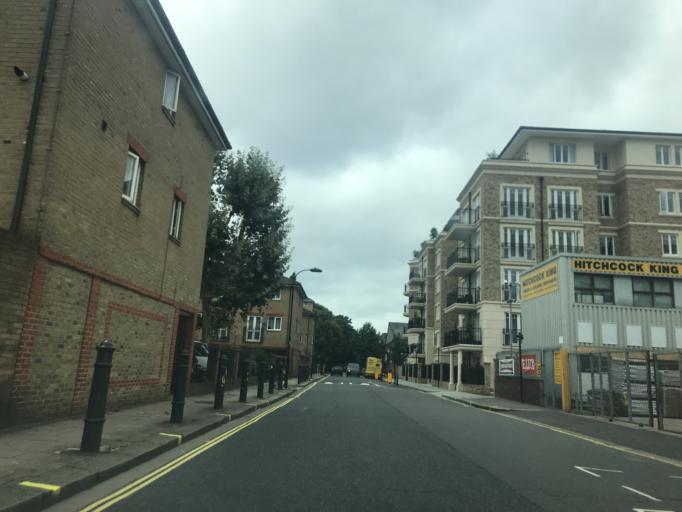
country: GB
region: England
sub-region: Greater London
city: Wandsworth
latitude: 51.4654
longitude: -0.1949
